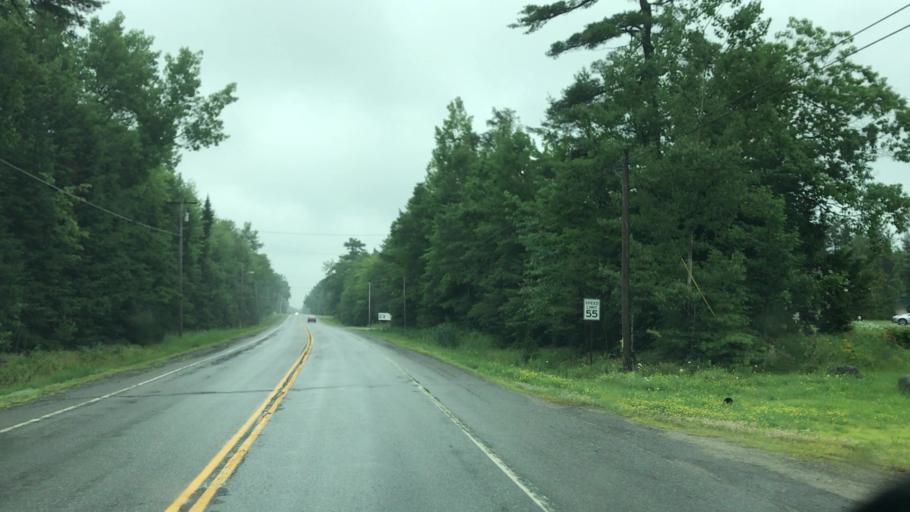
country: US
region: Maine
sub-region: Penobscot County
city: Howland
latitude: 45.2544
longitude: -68.6375
